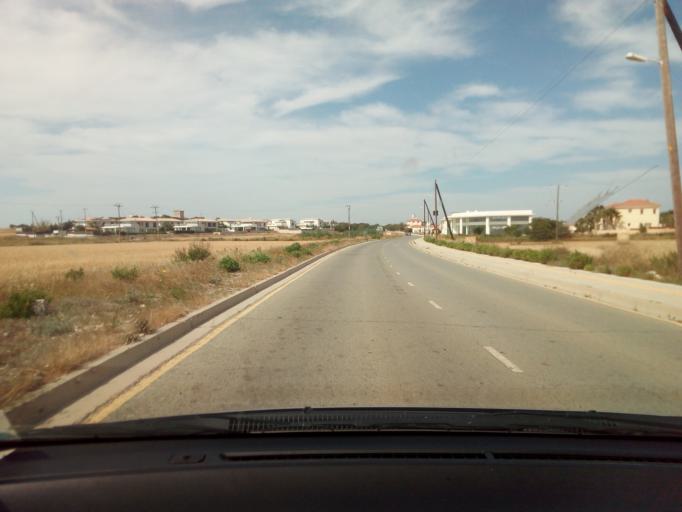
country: CY
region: Larnaka
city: Perivolia
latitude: 34.8284
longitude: 33.6019
